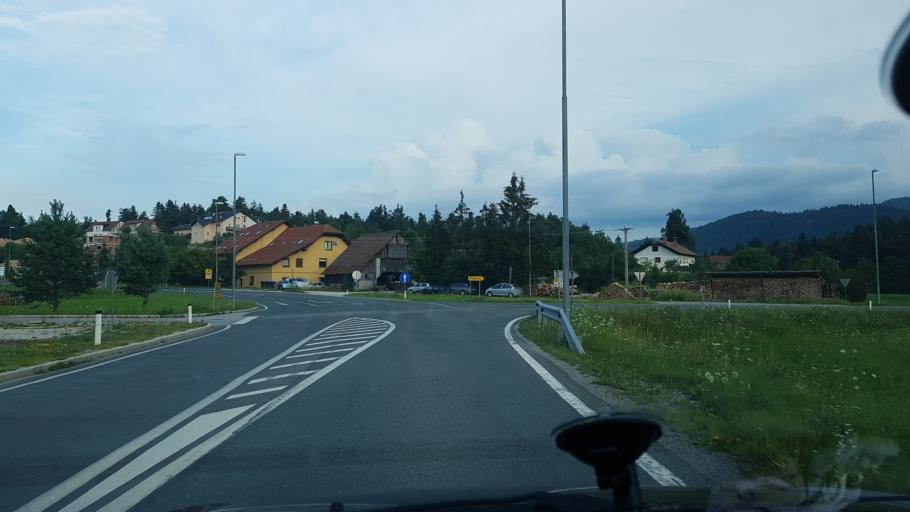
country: SI
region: Logatec
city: Logatec
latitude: 45.8954
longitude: 14.1891
